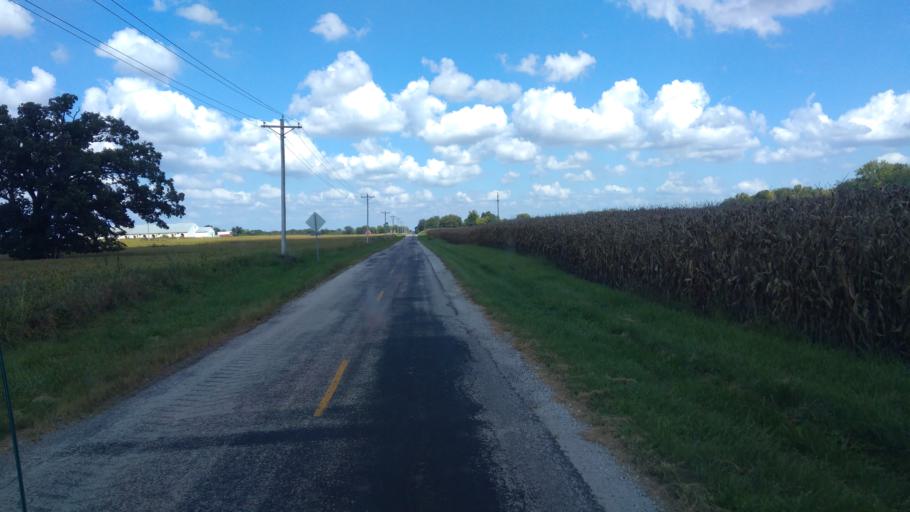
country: US
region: Ohio
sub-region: Wyandot County
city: Upper Sandusky
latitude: 40.6596
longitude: -83.3429
